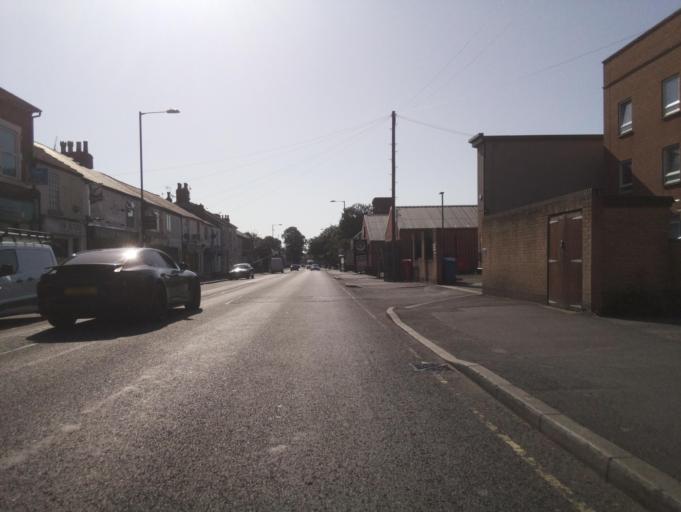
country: GB
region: England
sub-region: Derby
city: Derby
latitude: 52.9272
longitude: -1.4982
